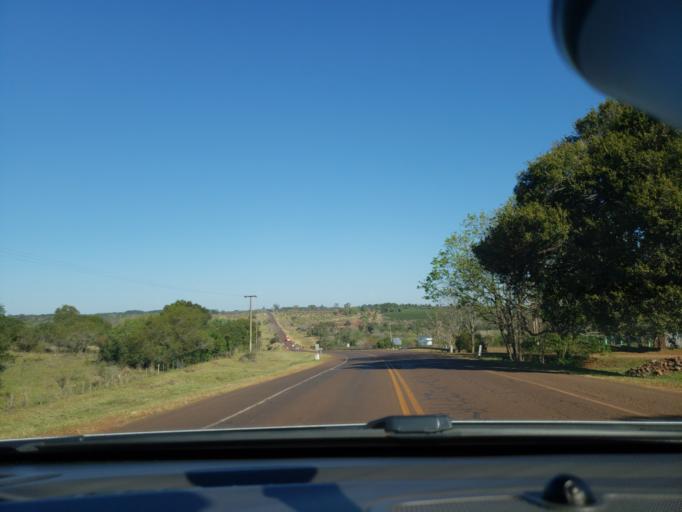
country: AR
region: Misiones
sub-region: Departamento de Apostoles
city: San Jose
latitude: -27.7740
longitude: -55.7734
